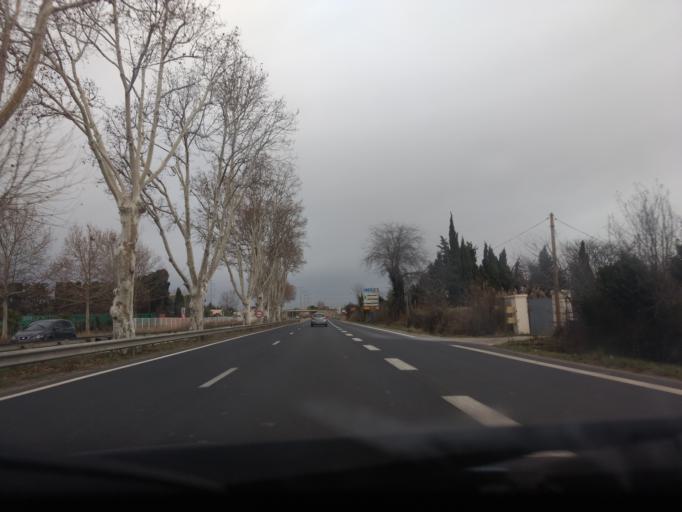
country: FR
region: Languedoc-Roussillon
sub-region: Departement de l'Herault
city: Lattes
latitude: 43.5772
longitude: 3.8976
